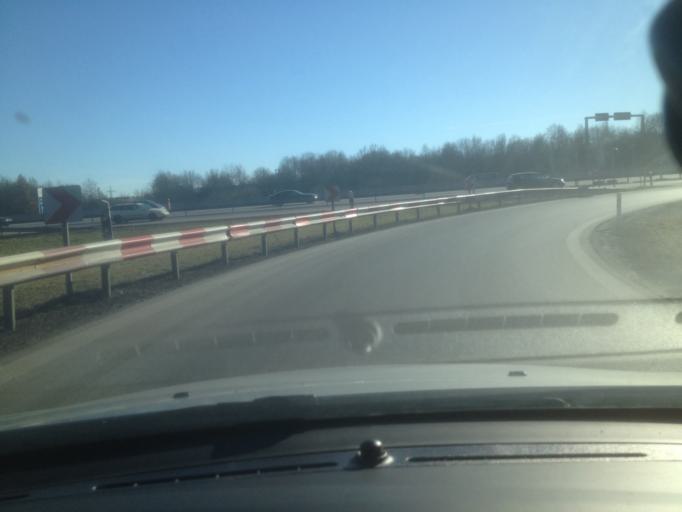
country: DE
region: Bavaria
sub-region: Swabia
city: Gersthofen
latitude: 48.4153
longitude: 10.8731
